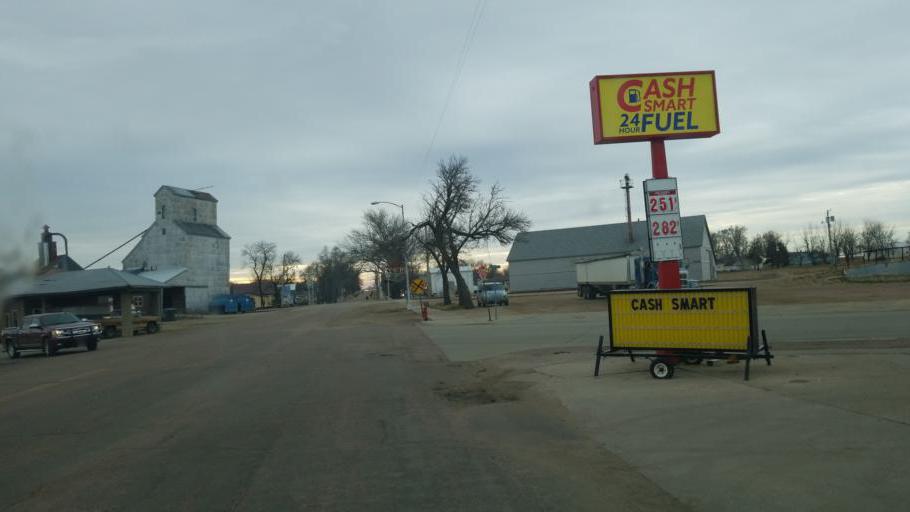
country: US
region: South Dakota
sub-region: Hutchinson County
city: Parkston
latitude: 43.2239
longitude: -97.9657
